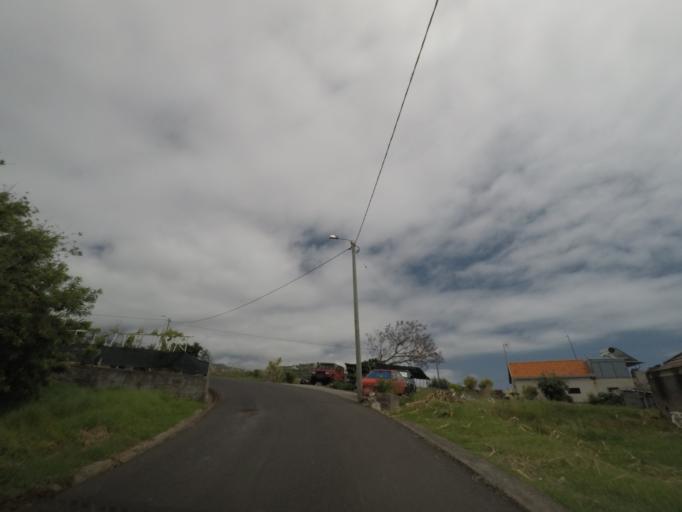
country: PT
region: Madeira
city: Ponta do Sol
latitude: 32.6853
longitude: -17.1020
